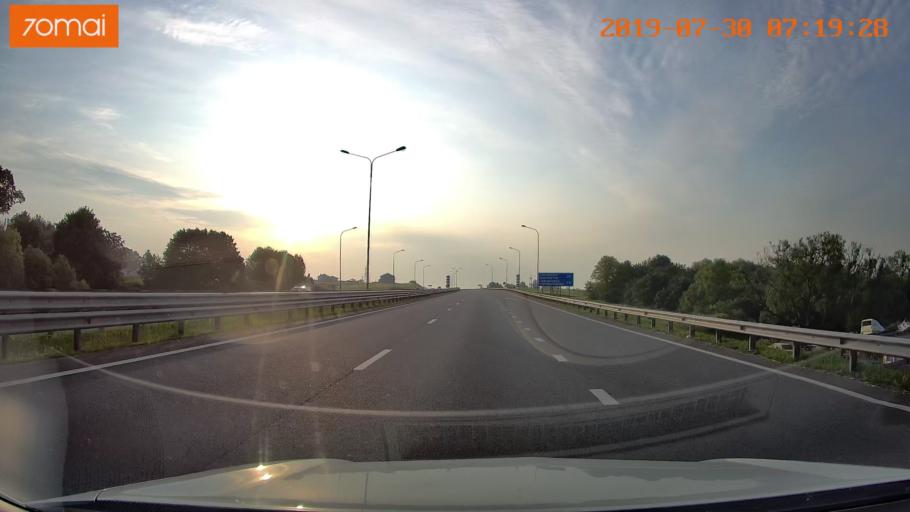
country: RU
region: Kaliningrad
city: Bol'shoe Isakovo
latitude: 54.7012
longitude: 20.6750
